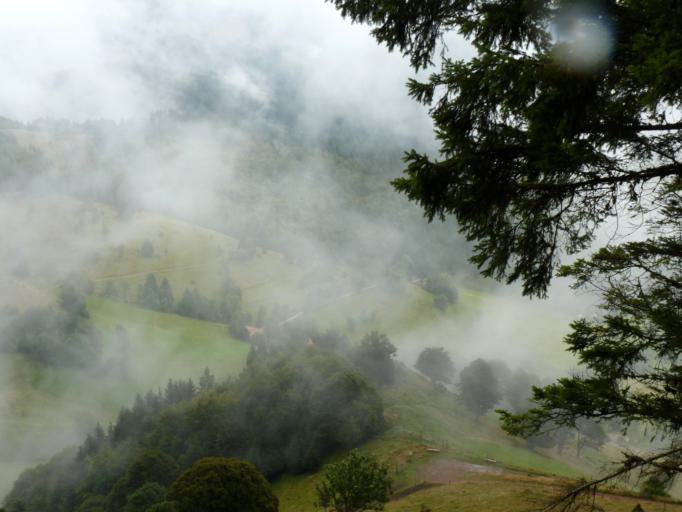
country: DE
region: Baden-Wuerttemberg
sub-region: Freiburg Region
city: Bollen
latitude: 47.8167
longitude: 7.8239
